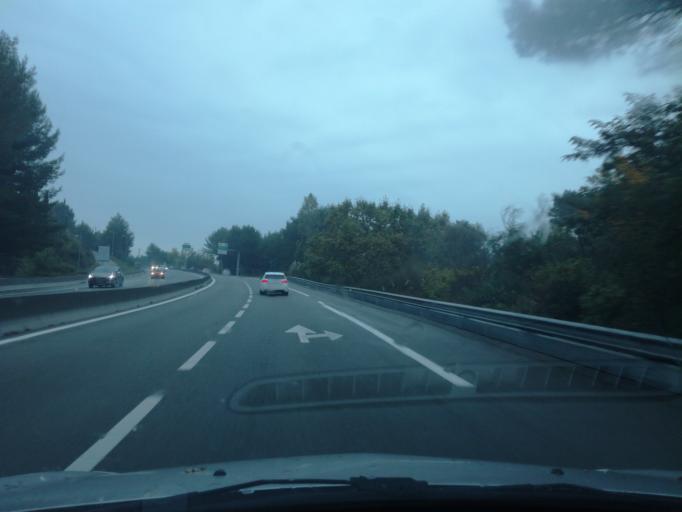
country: FR
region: Provence-Alpes-Cote d'Azur
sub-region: Departement des Alpes-Maritimes
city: Mougins
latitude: 43.5993
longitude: 7.0023
